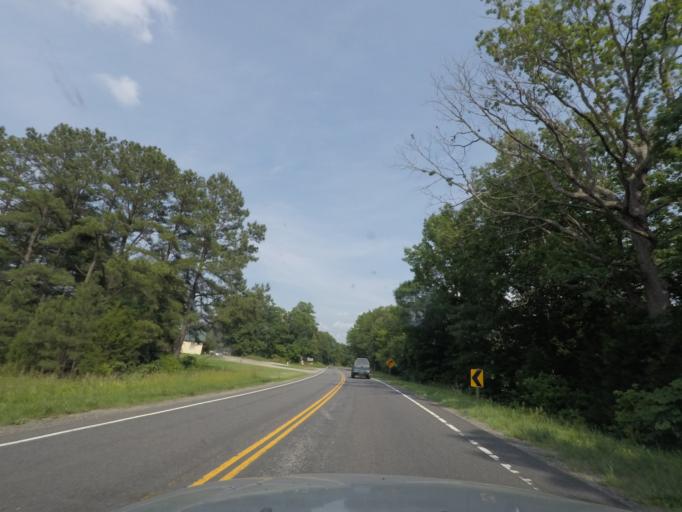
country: US
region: Virginia
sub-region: Buckingham County
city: Buckingham
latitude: 37.5066
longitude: -78.4832
